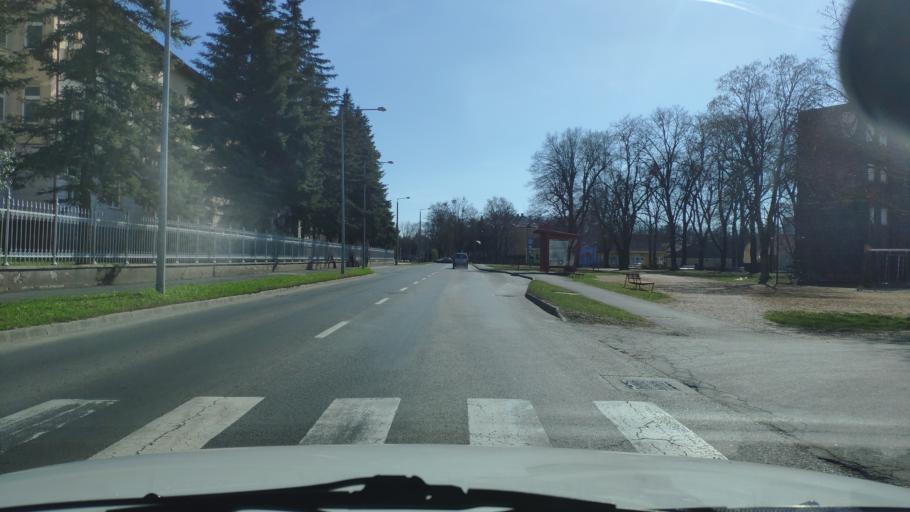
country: HU
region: Zala
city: Nagykanizsa
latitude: 46.4528
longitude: 16.9976
